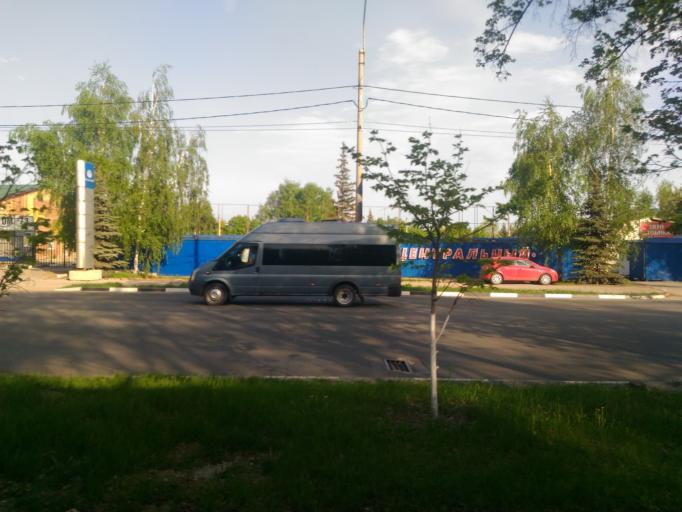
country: RU
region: Ulyanovsk
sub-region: Ulyanovskiy Rayon
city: Ulyanovsk
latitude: 54.2997
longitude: 48.3814
